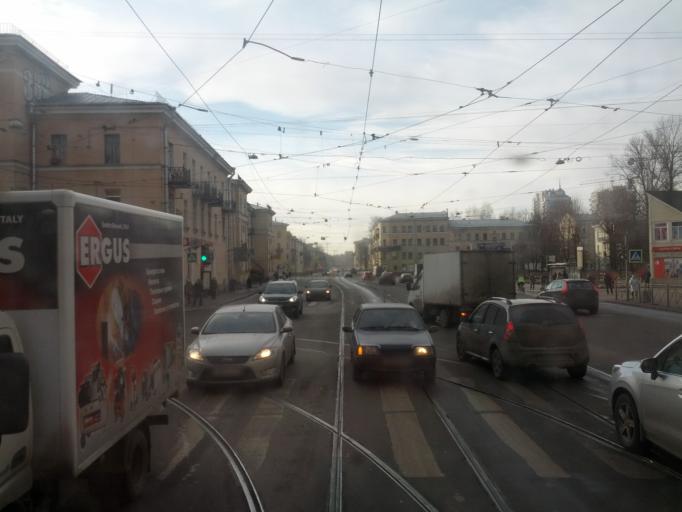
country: RU
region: Leningrad
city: Kalininskiy
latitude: 59.9536
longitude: 30.4151
